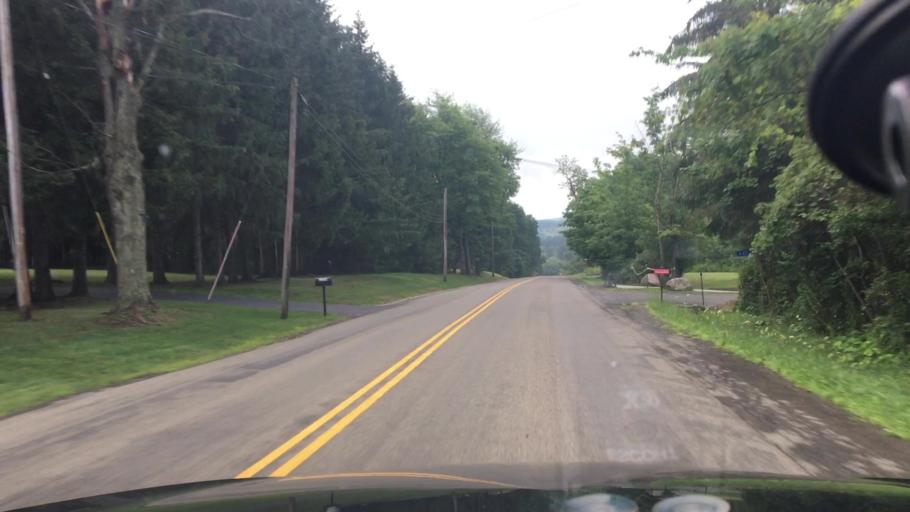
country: US
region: New York
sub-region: Chautauqua County
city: Lakewood
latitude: 42.1008
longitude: -79.3785
